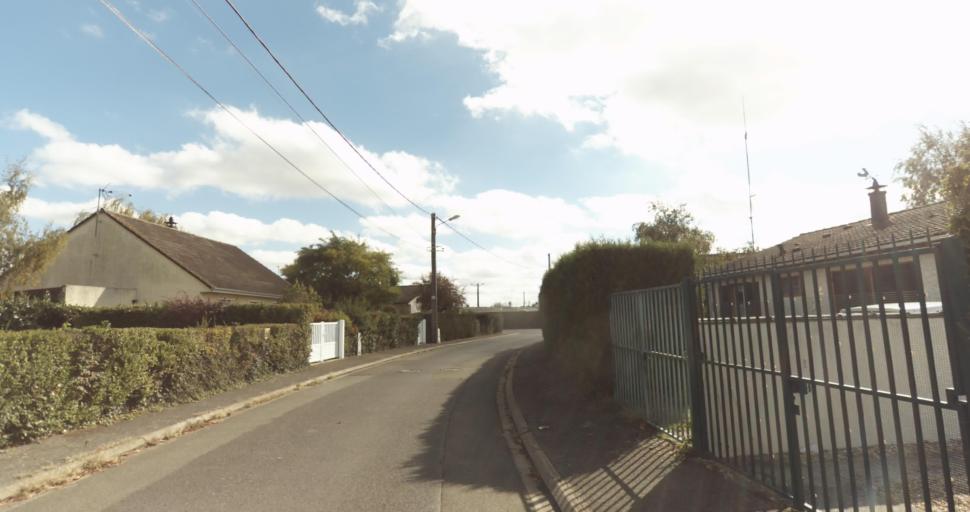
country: FR
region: Centre
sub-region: Departement d'Eure-et-Loir
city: Garnay
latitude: 48.7318
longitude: 1.3286
